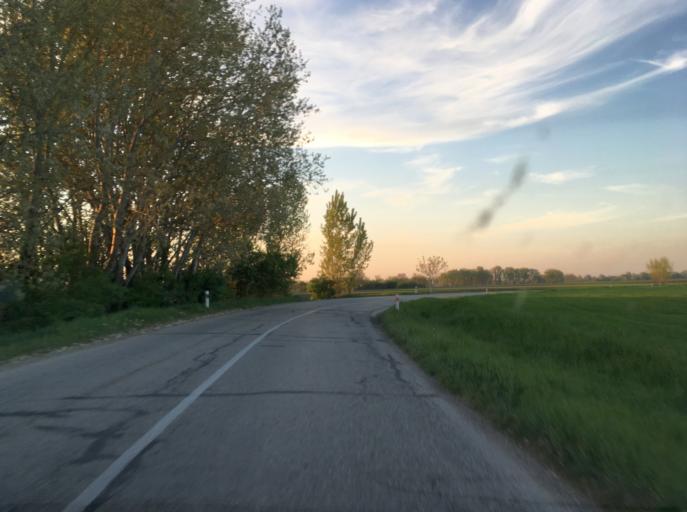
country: SK
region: Nitriansky
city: Kolarovo
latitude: 47.8780
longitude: 17.9179
